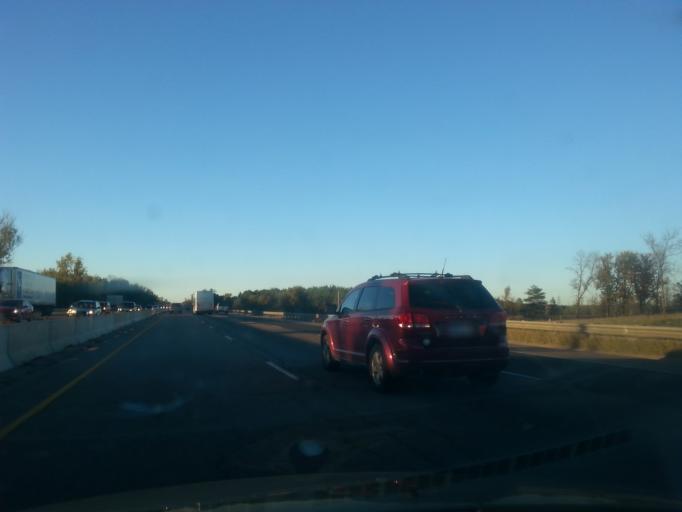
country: CA
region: Ontario
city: Innisfil
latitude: 44.2169
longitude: -79.6615
